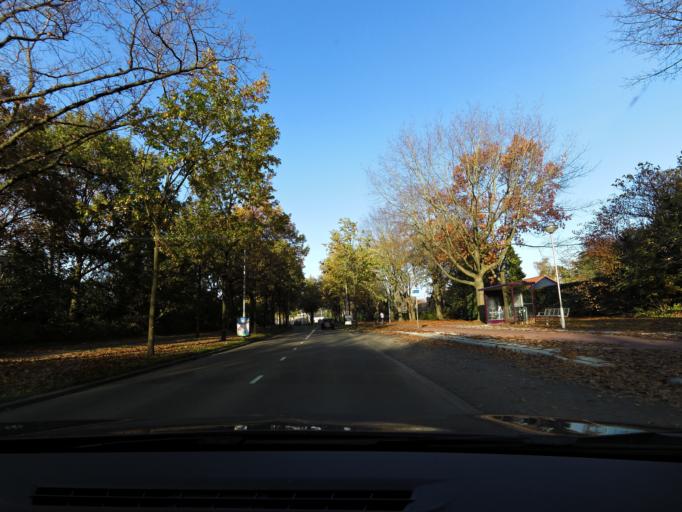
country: NL
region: North Brabant
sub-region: Gemeente Breda
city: Breda
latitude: 51.5636
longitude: 4.7932
